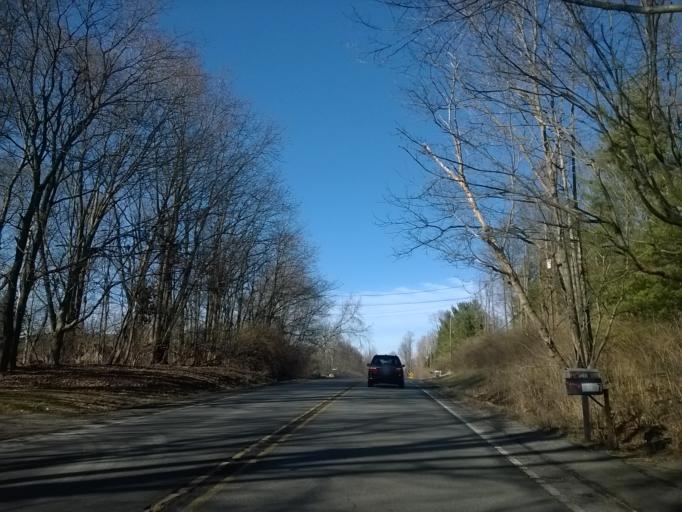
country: US
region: Indiana
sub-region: Boone County
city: Zionsville
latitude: 39.9665
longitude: -86.2492
